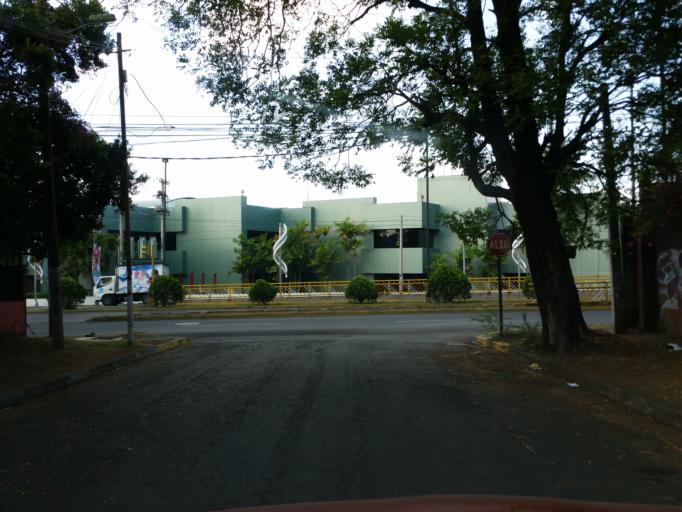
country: NI
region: Managua
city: Managua
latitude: 12.1148
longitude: -86.2571
